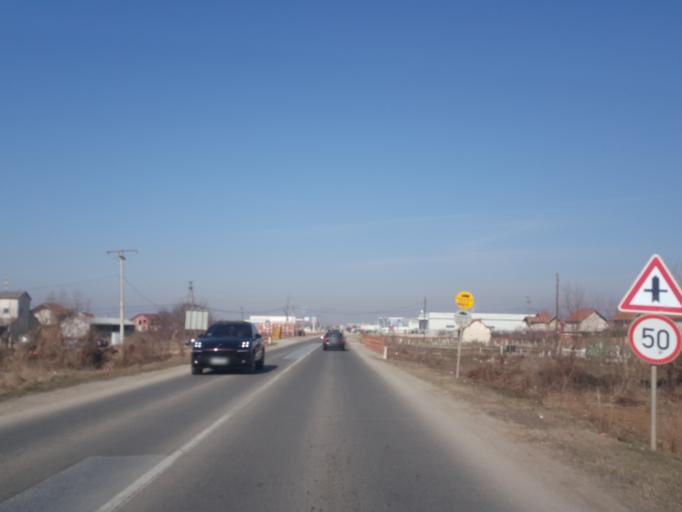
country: XK
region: Mitrovica
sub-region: Vushtrri
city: Vushtrri
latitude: 42.7812
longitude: 21.0128
